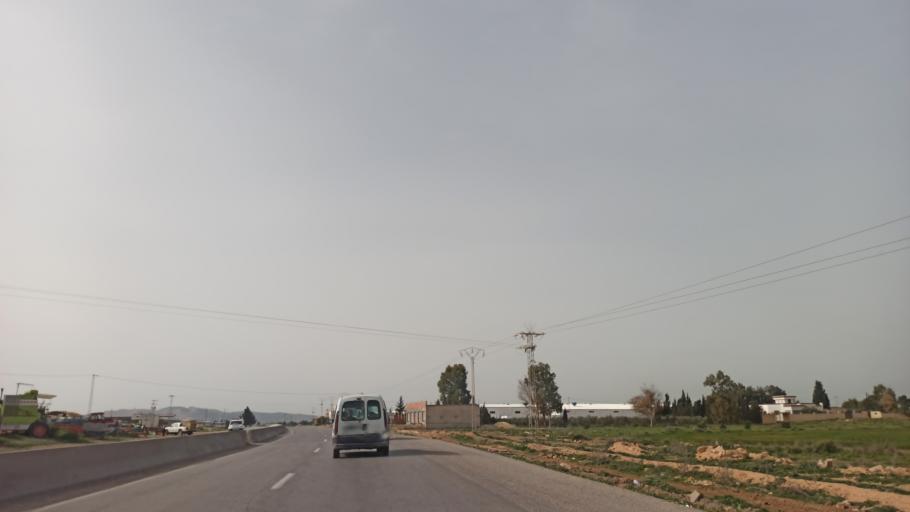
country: TN
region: Tunis
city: La Mohammedia
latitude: 36.5864
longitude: 10.1007
